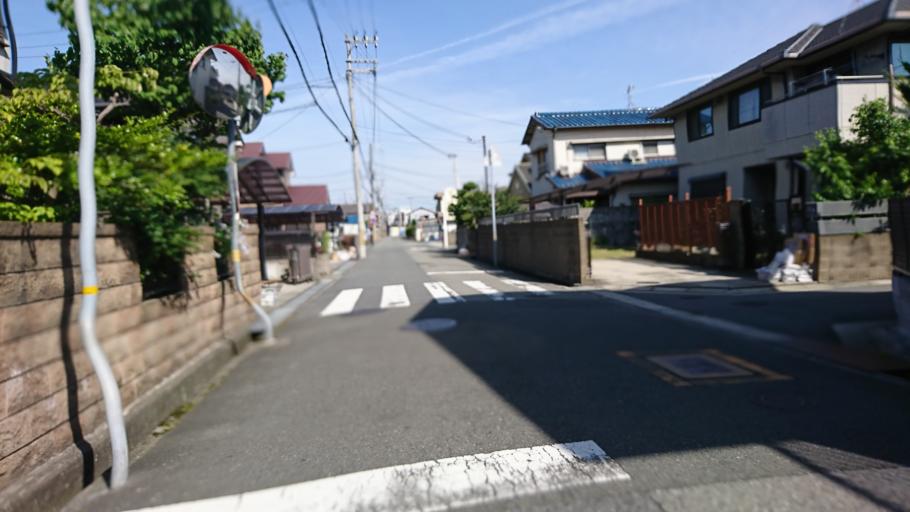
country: JP
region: Hyogo
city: Kakogawacho-honmachi
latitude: 34.7638
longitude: 134.7991
